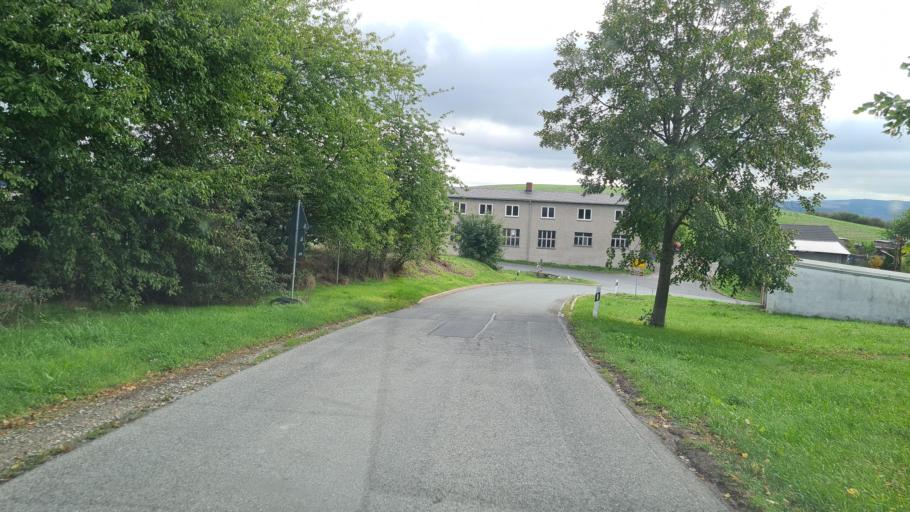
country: DE
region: Thuringia
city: Leutenberg
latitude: 50.5644
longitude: 11.4231
